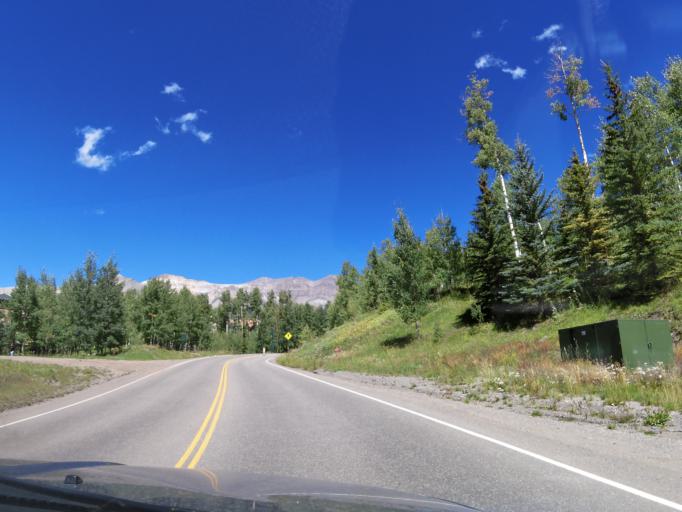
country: US
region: Colorado
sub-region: San Miguel County
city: Mountain Village
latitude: 37.9333
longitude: -107.8491
